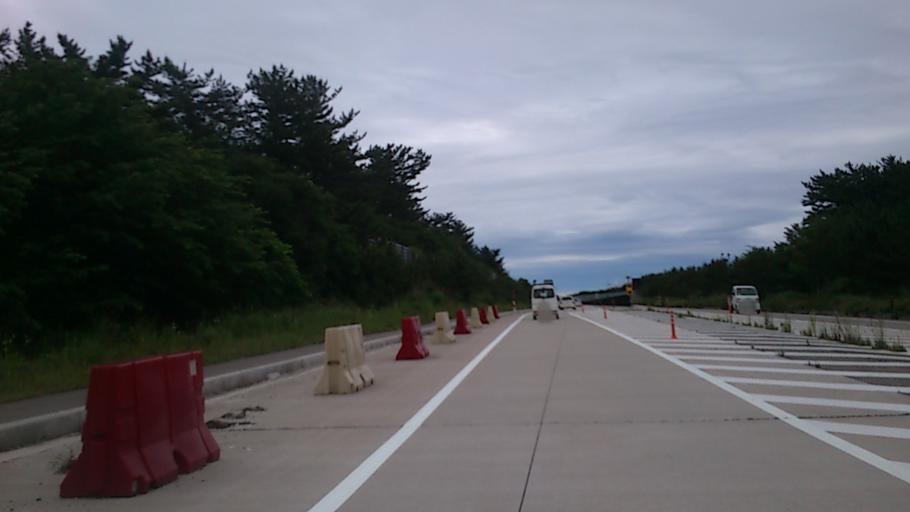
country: JP
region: Akita
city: Akita Shi
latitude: 39.7068
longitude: 140.0719
